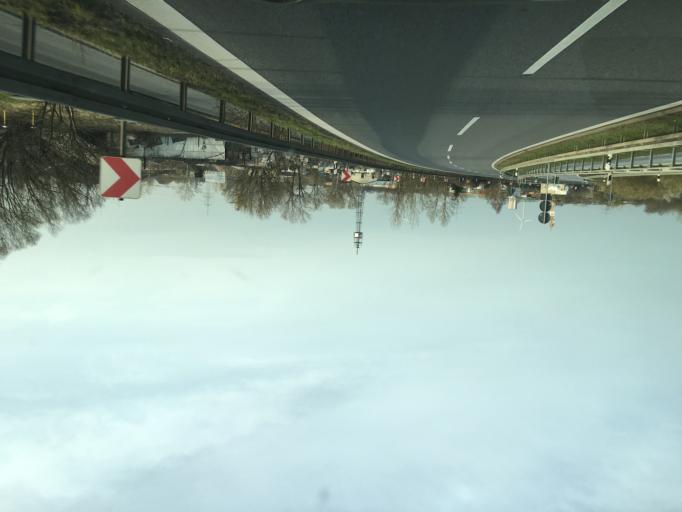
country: DE
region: Berlin
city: Buchholz
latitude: 52.6458
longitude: 13.4263
